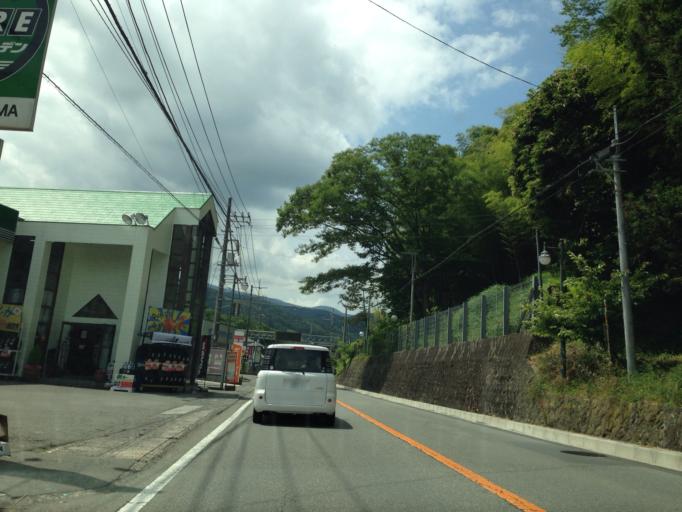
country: JP
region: Shizuoka
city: Heda
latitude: 34.9333
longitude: 138.9334
